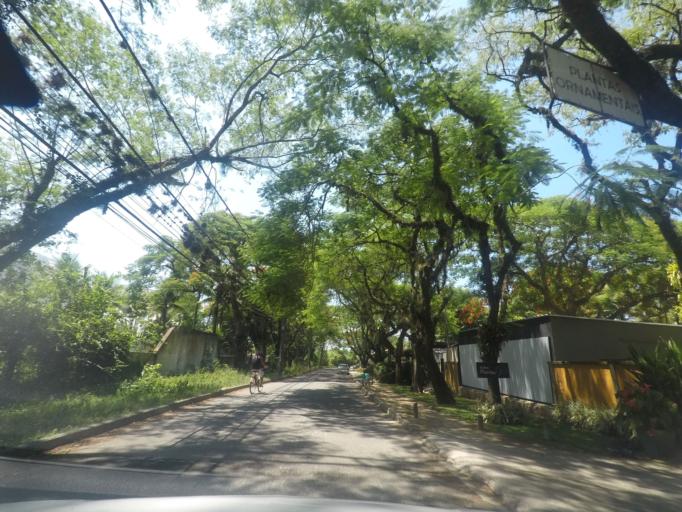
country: BR
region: Rio de Janeiro
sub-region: Nilopolis
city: Nilopolis
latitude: -22.9828
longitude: -43.4591
